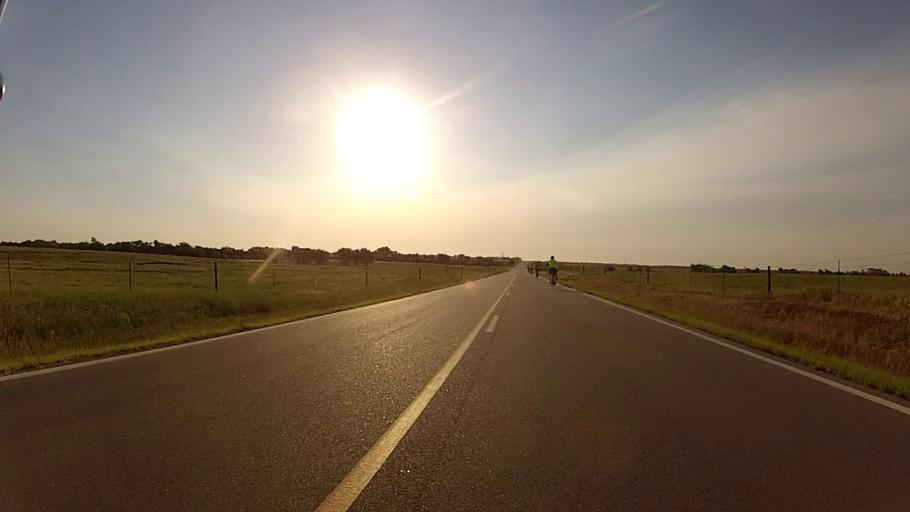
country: US
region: Kansas
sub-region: Harper County
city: Anthony
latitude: 37.1545
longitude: -97.8059
